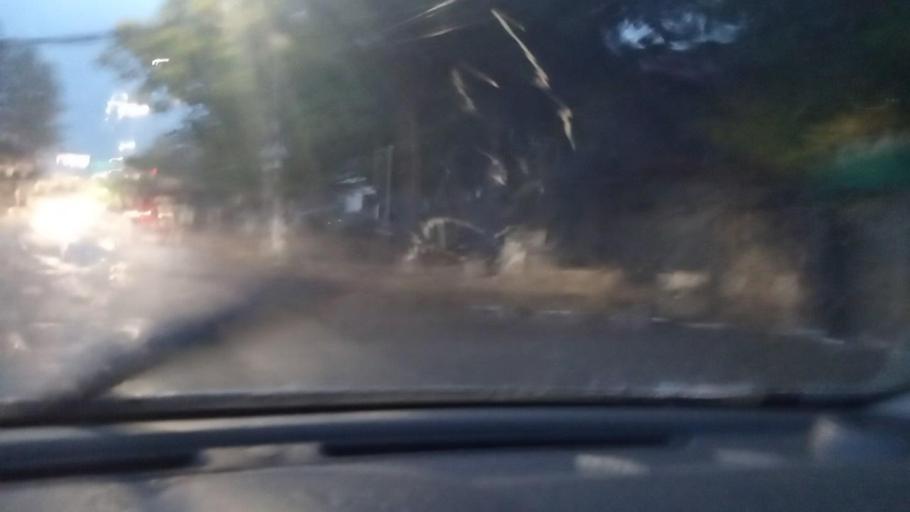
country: UZ
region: Toshkent
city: Salor
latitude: 41.3223
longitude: 69.3456
